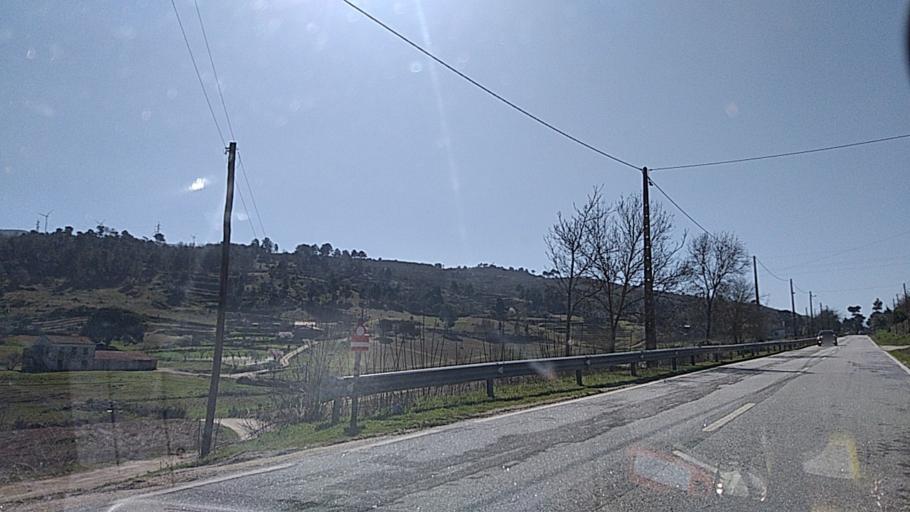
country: PT
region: Guarda
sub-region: Celorico da Beira
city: Celorico da Beira
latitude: 40.6123
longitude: -7.4147
